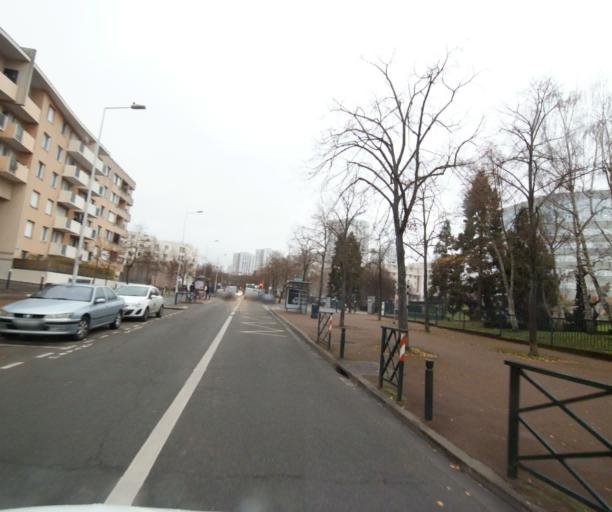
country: FR
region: Ile-de-France
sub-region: Departement des Hauts-de-Seine
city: Nanterre
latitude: 48.8916
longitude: 2.2148
